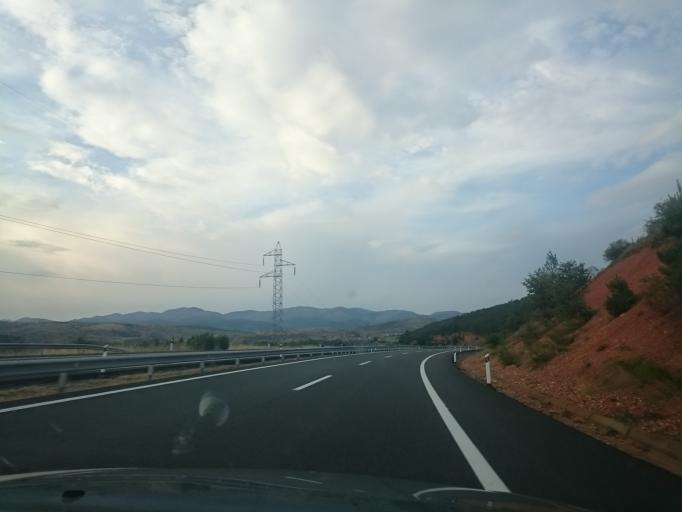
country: ES
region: Castille and Leon
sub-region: Provincia de Leon
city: Santa Maria de Ordas
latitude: 42.7237
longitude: -5.7897
